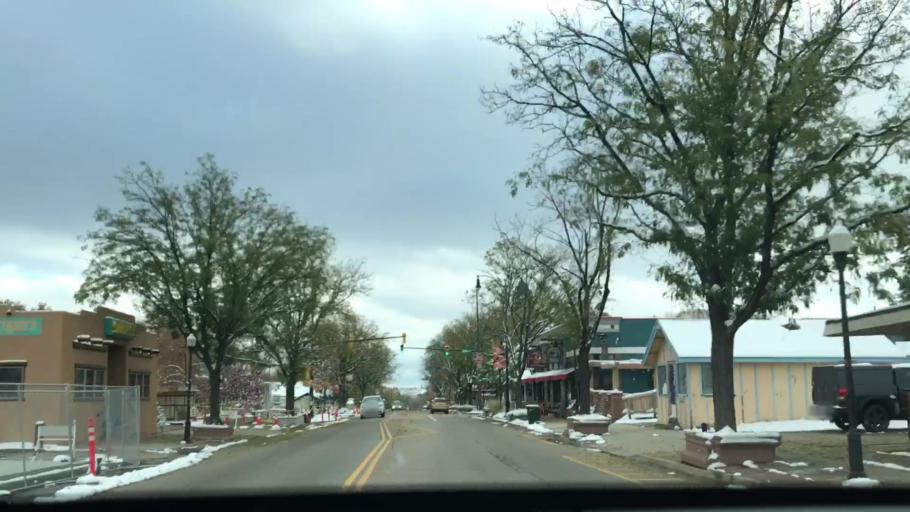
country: US
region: Colorado
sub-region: Boulder County
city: Lafayette
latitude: 39.9990
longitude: -105.0905
